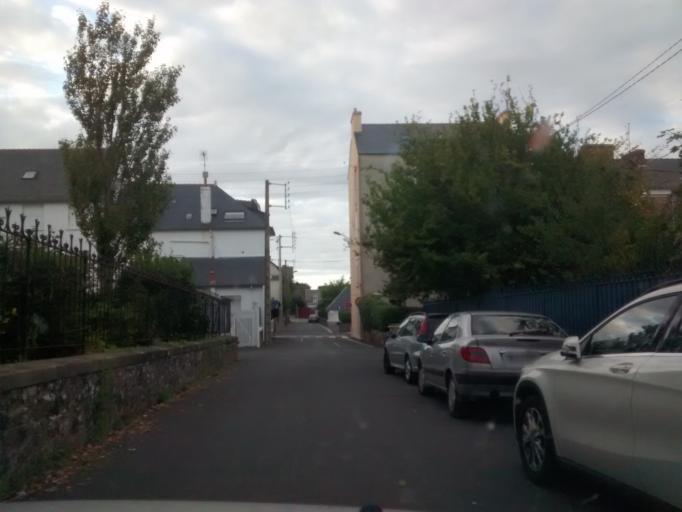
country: FR
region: Brittany
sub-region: Departement d'Ille-et-Vilaine
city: Saint-Lunaire
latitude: 48.6360
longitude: -2.1121
